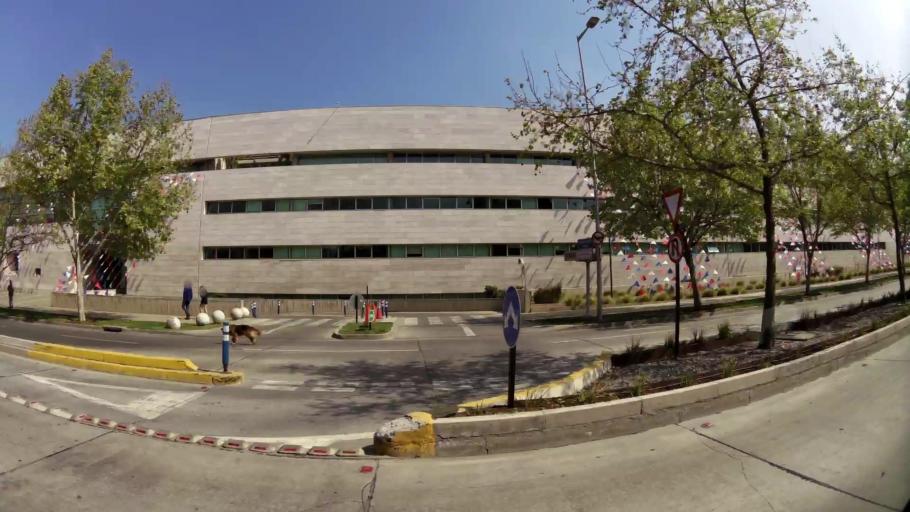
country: CL
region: Santiago Metropolitan
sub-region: Provincia de Santiago
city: Villa Presidente Frei, Nunoa, Santiago, Chile
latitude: -33.3992
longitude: -70.6011
